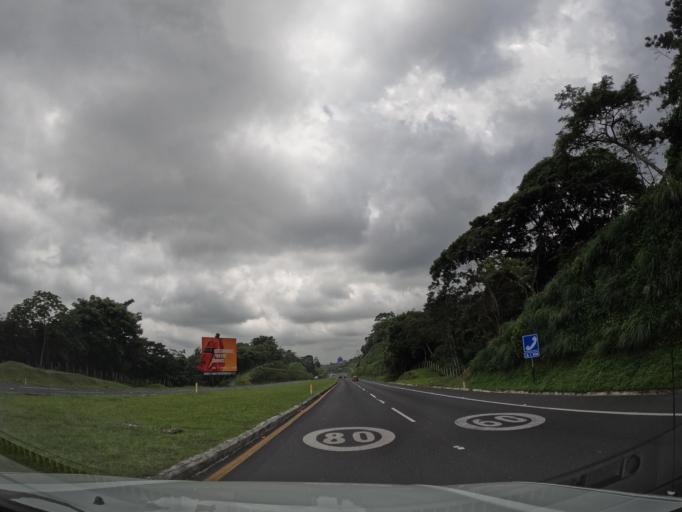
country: GT
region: Escuintla
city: Palin
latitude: 14.3930
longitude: -90.7434
